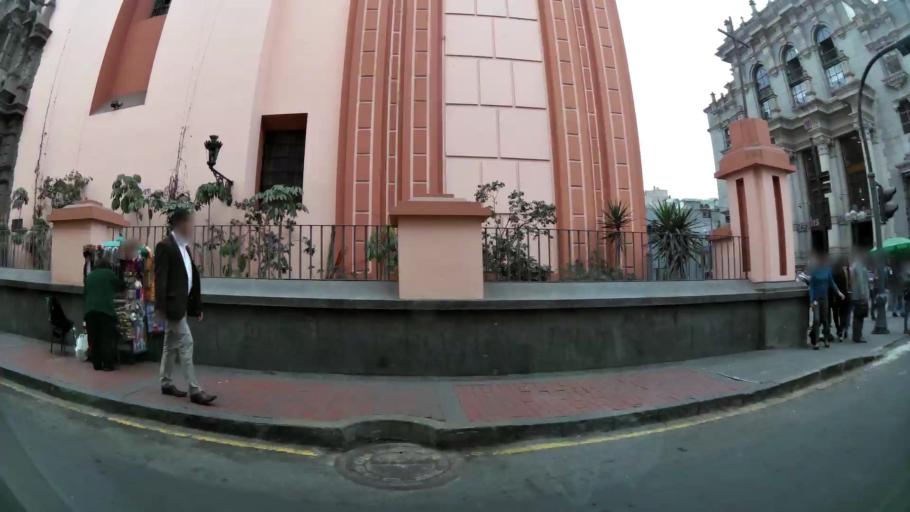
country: PE
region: Lima
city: Lima
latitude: -12.0481
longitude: -77.0327
